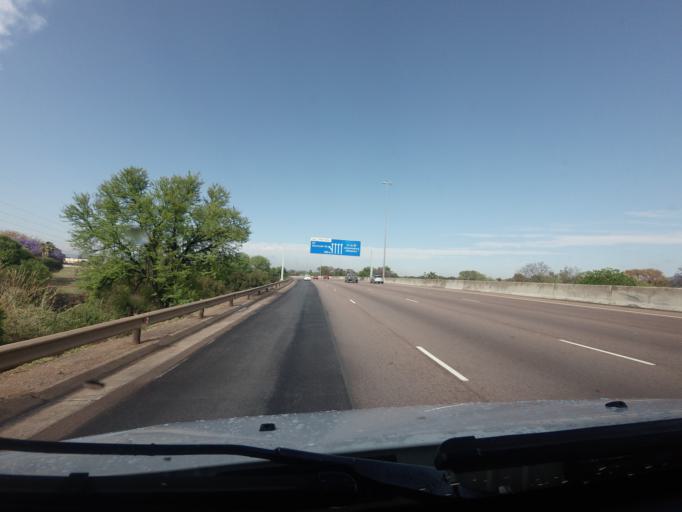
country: ZA
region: Gauteng
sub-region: City of Tshwane Metropolitan Municipality
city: Pretoria
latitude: -25.7033
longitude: 28.2713
